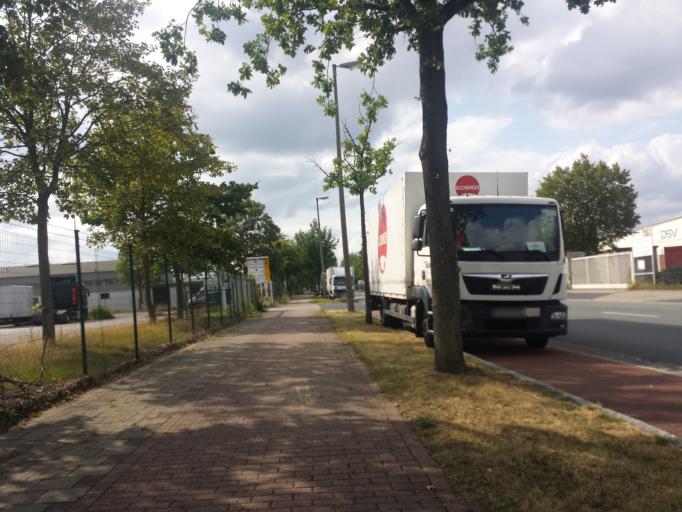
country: DE
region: Lower Saxony
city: Stuhr
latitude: 53.0820
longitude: 8.7281
